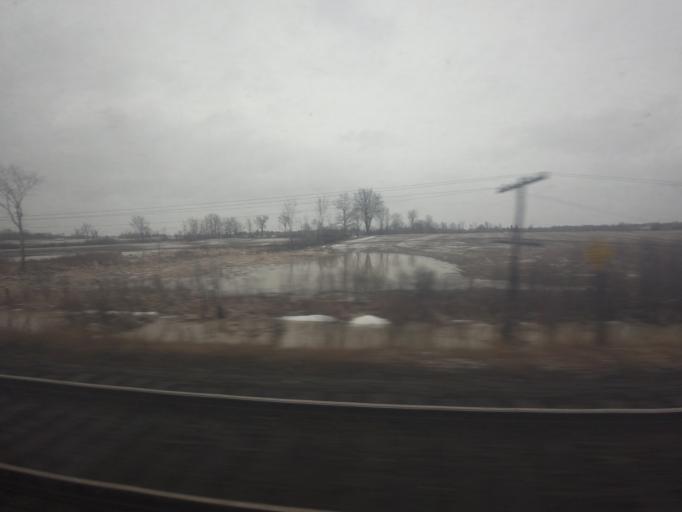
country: CA
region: Ontario
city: Gananoque
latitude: 44.3357
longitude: -76.3006
